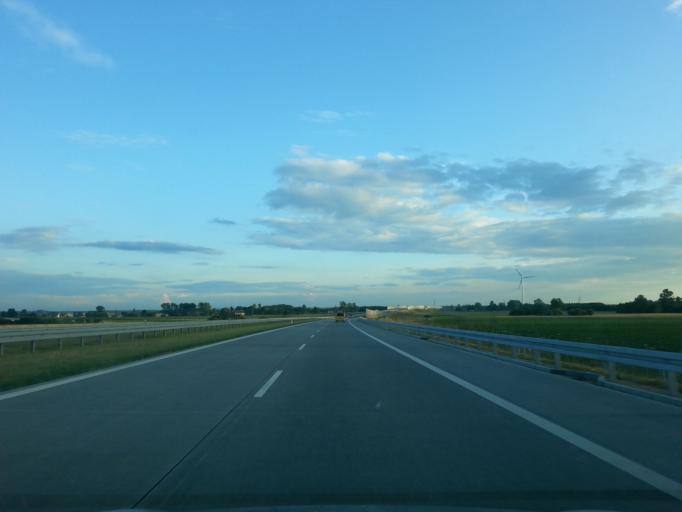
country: PL
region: Lodz Voivodeship
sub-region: Powiat sieradzki
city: Zloczew
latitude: 51.4173
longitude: 18.6423
